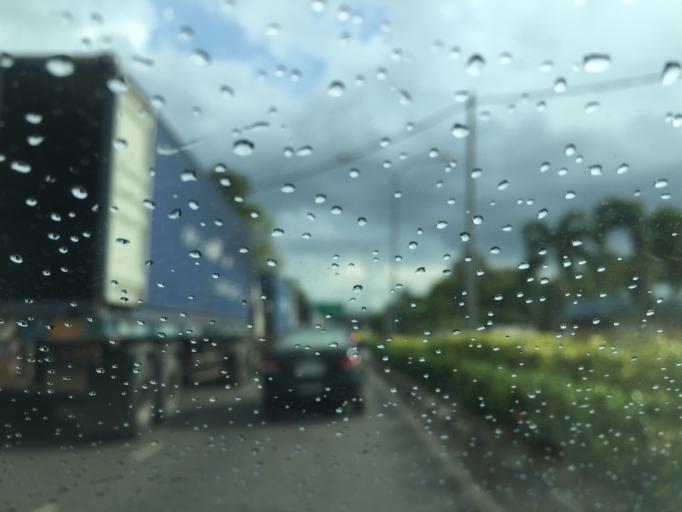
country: TH
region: Songkhla
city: Sadao
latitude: 6.5161
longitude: 100.4196
